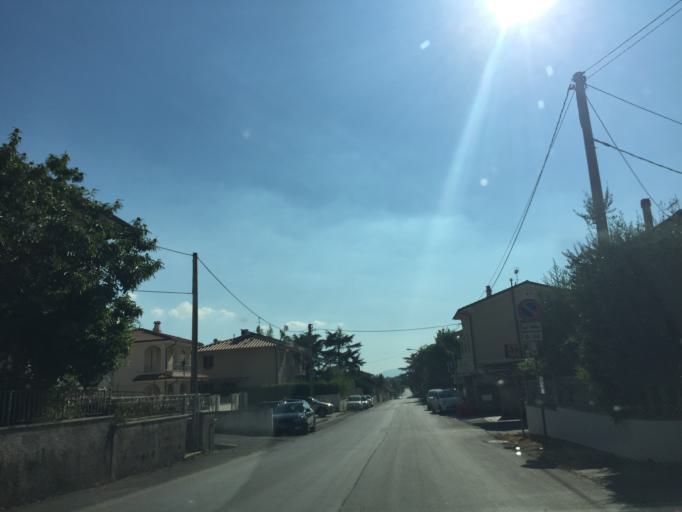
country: IT
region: Tuscany
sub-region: Provincia di Pistoia
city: San Rocco
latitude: 43.8175
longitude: 10.8604
